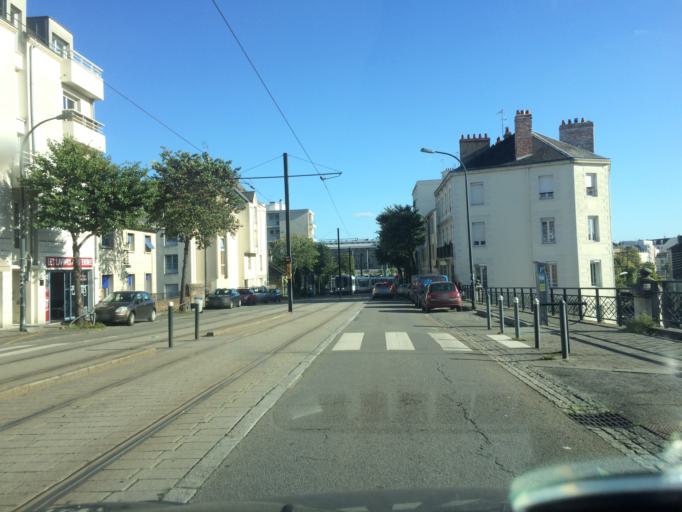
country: FR
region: Pays de la Loire
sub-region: Departement de la Loire-Atlantique
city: Nantes
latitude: 47.2295
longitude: -1.5548
